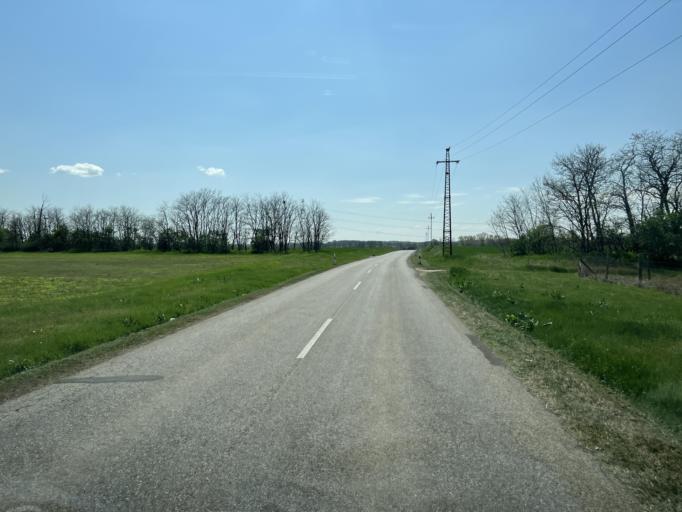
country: HU
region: Pest
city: Inarcs
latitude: 47.2360
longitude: 19.3105
